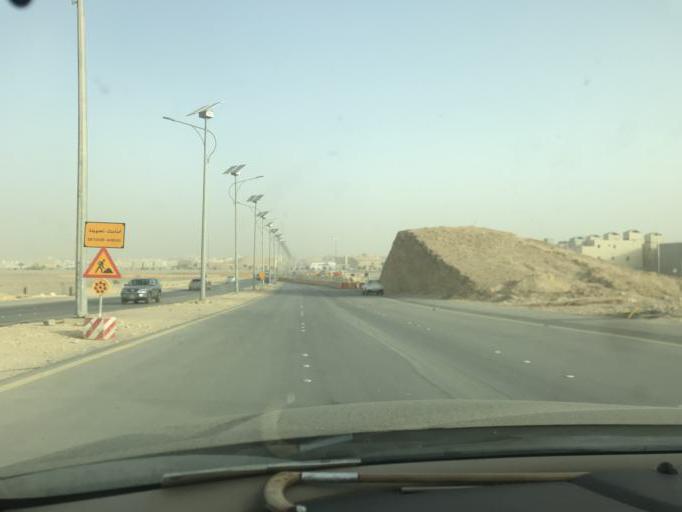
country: SA
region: Ar Riyad
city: Riyadh
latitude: 24.8433
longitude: 46.6655
